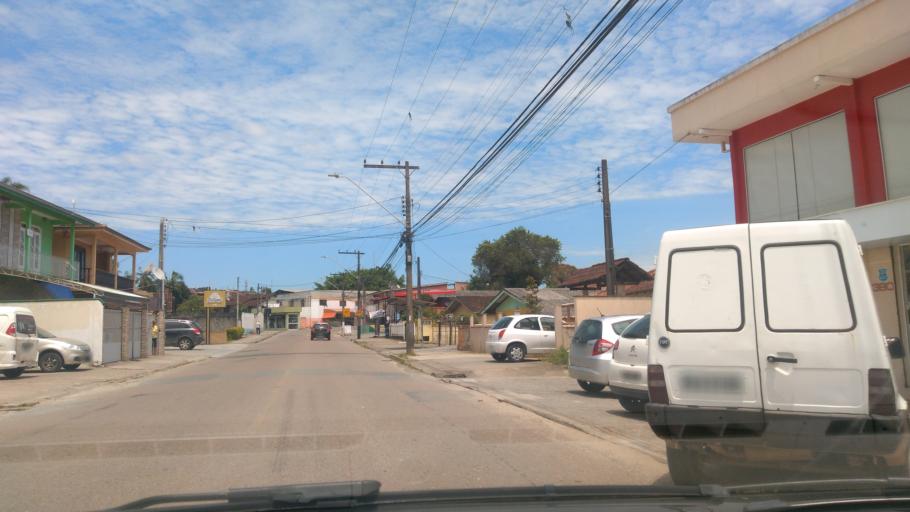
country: BR
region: Santa Catarina
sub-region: Joinville
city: Joinville
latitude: -26.3279
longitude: -48.8100
